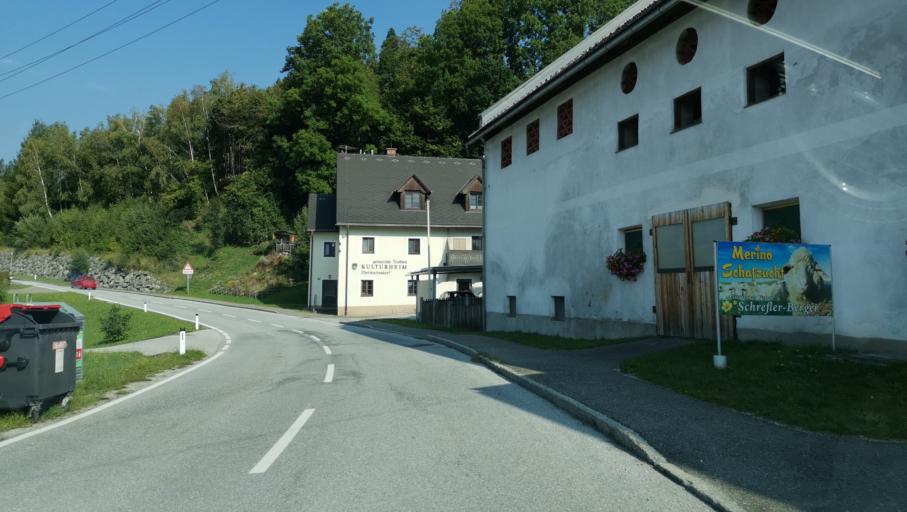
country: AT
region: Styria
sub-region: Politischer Bezirk Liezen
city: Trieben
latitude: 47.5044
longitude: 14.4765
